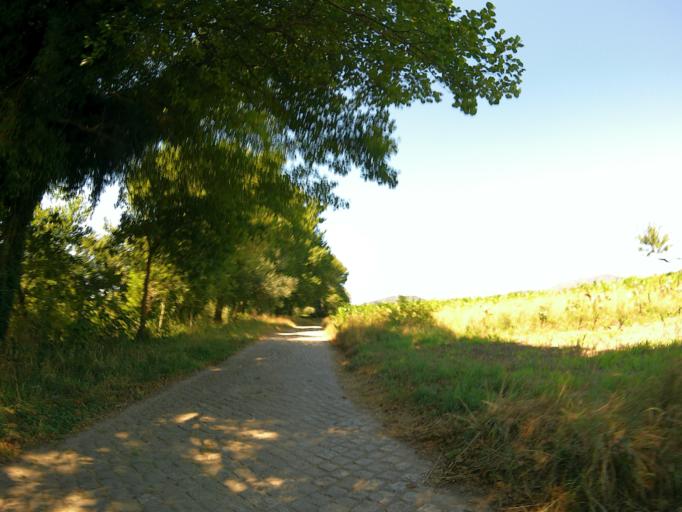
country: PT
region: Viana do Castelo
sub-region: Viana do Castelo
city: Darque
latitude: 41.7255
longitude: -8.6885
